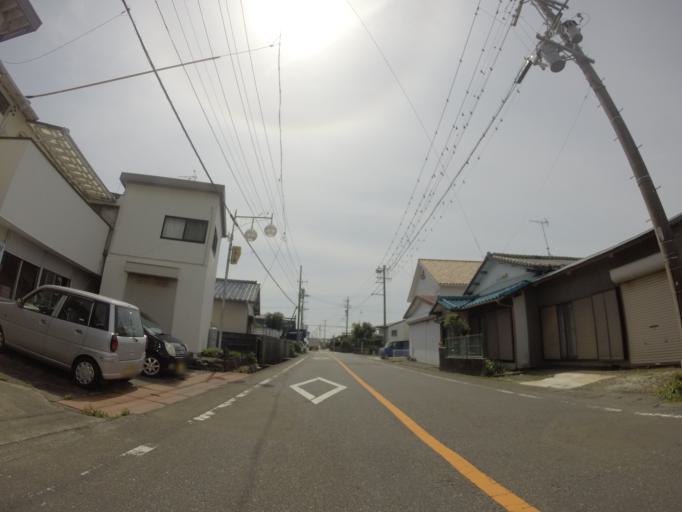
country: JP
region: Shizuoka
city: Fujieda
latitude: 34.8114
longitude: 138.2834
